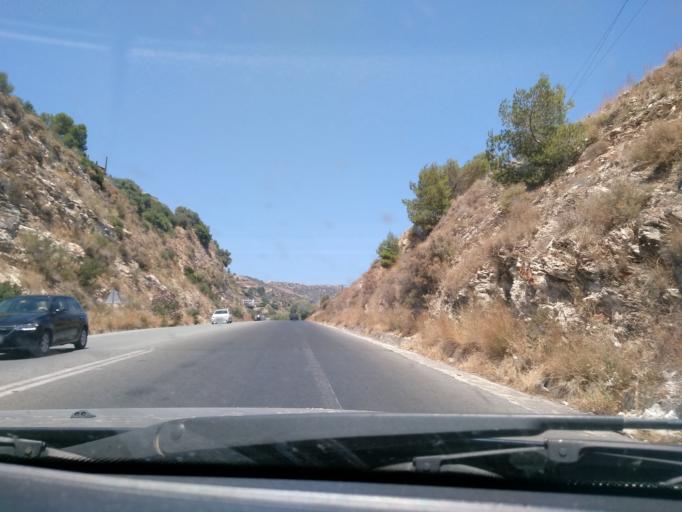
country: GR
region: Crete
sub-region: Nomos Irakleiou
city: Gazi
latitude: 35.3555
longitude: 25.0402
